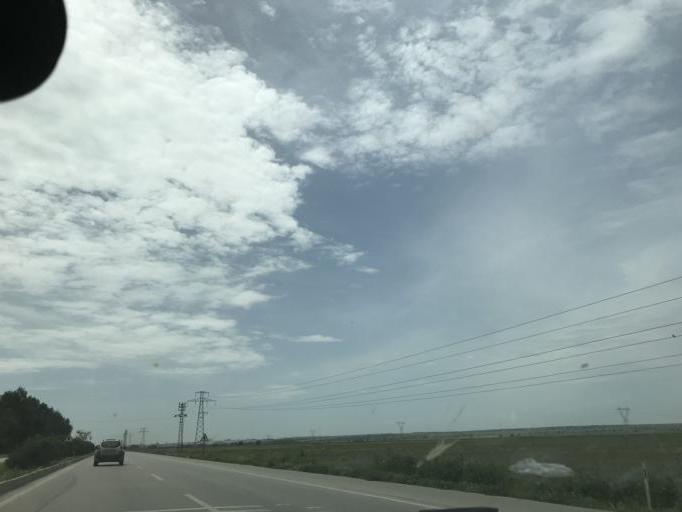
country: TR
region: Adana
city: Ceyhan
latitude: 37.0260
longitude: 35.7314
